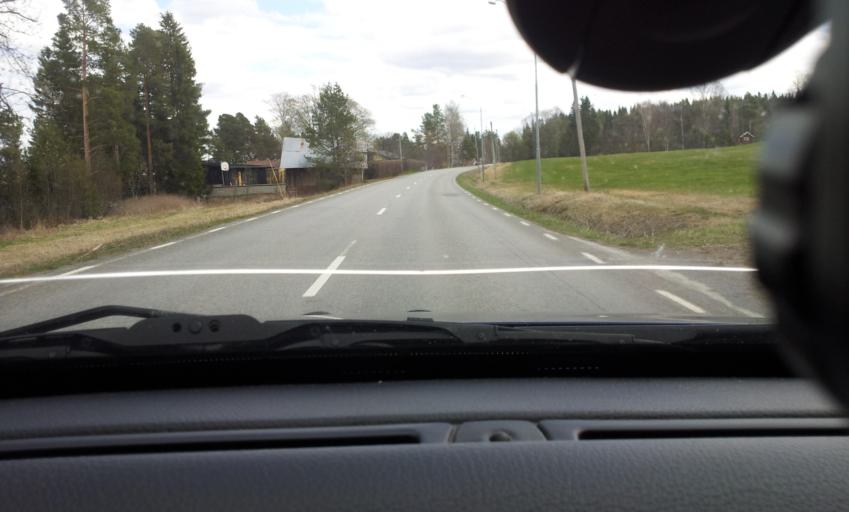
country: SE
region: Jaemtland
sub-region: OEstersunds Kommun
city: Ostersund
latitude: 63.1318
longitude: 14.6630
